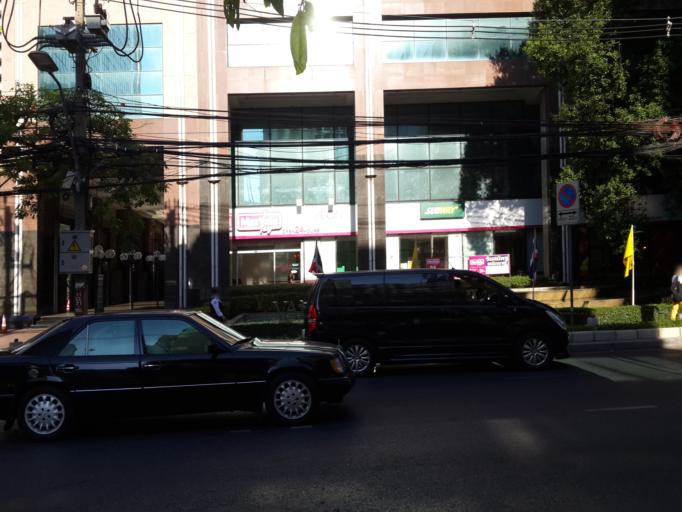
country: TH
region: Bangkok
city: Ratchathewi
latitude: 13.7458
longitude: 100.5443
